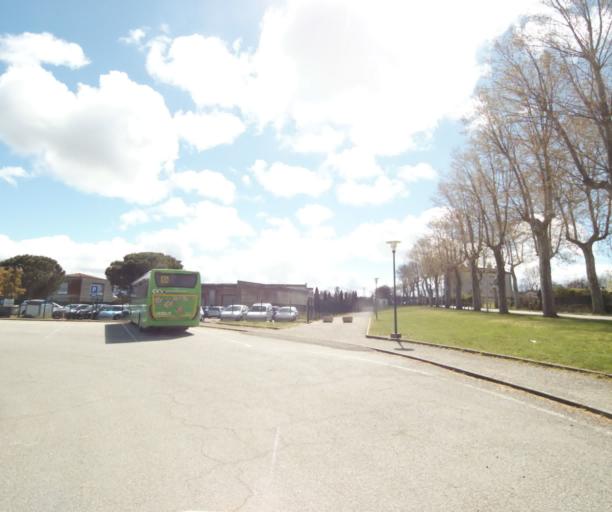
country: FR
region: Midi-Pyrenees
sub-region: Departement de l'Ariege
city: Saverdun
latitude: 43.2408
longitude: 1.5721
